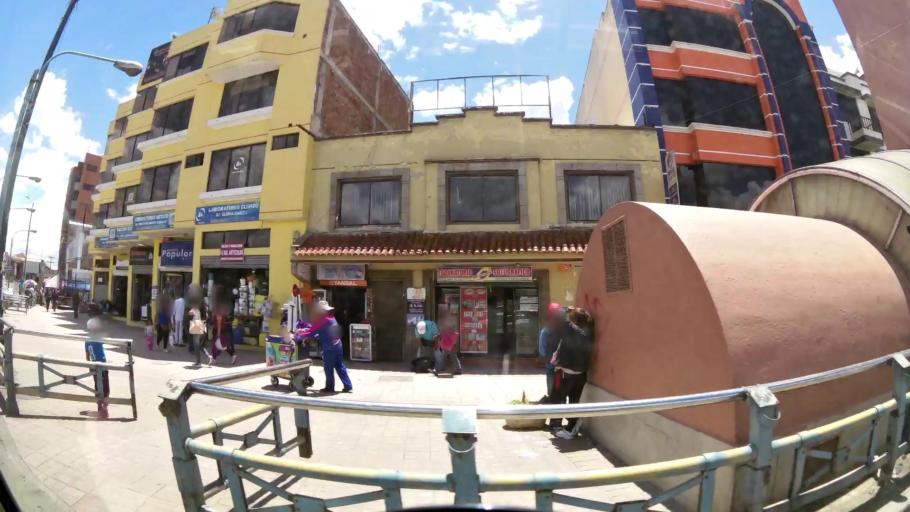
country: EC
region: Azuay
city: Cuenca
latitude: -2.8978
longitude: -79.0258
